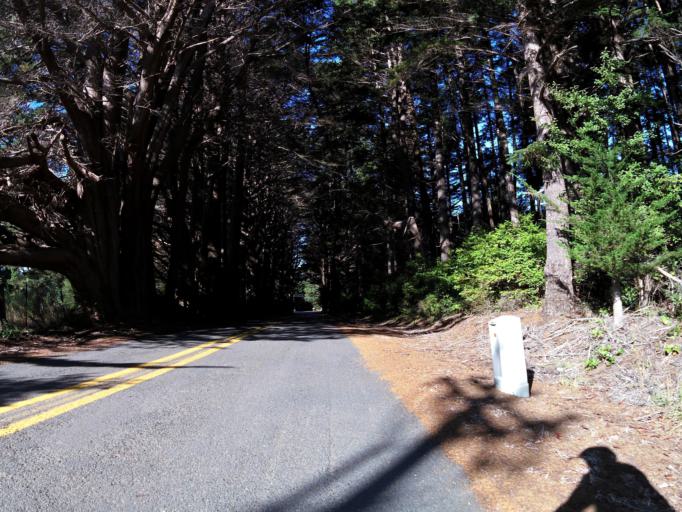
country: US
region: Oregon
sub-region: Coos County
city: Bandon
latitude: 43.0398
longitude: -124.4128
